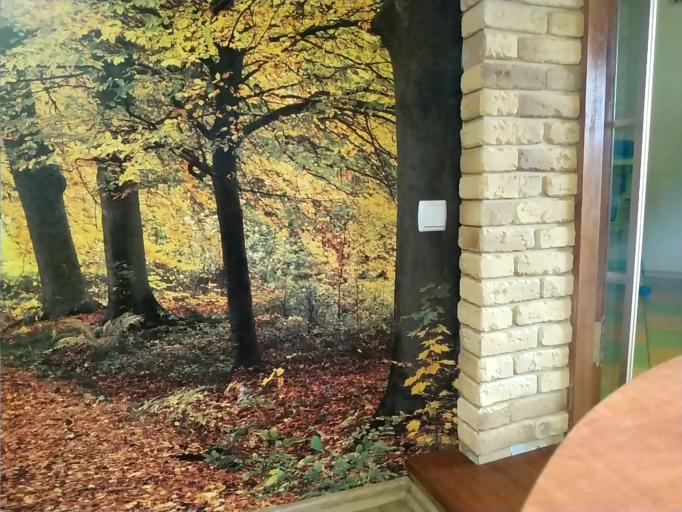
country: RU
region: Smolensk
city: Dorogobuzh
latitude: 54.8597
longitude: 33.3153
